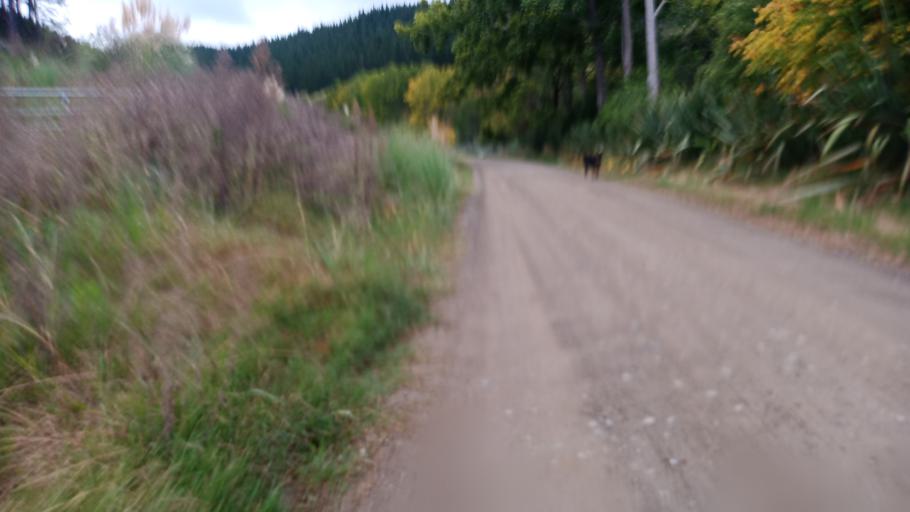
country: NZ
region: Gisborne
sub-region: Gisborne District
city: Gisborne
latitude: -38.6500
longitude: 178.0401
